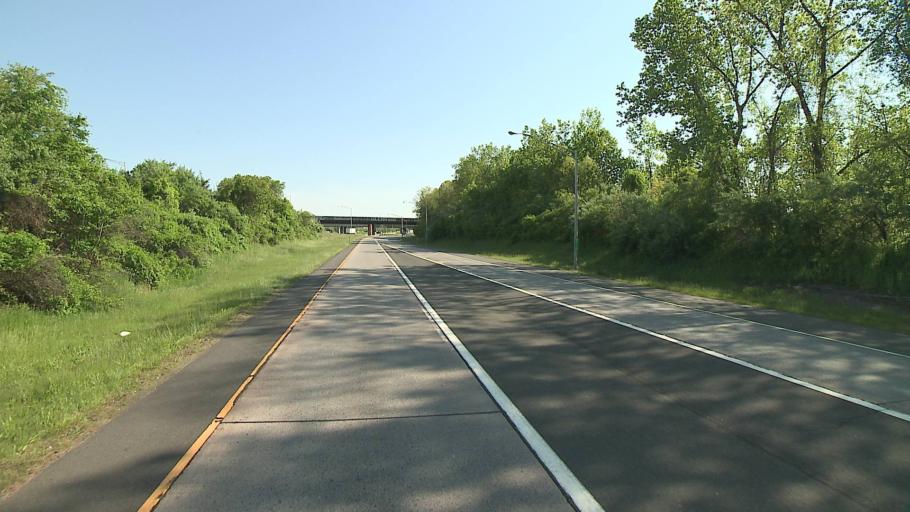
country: US
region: Connecticut
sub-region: Hartford County
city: Manchester
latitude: 41.7927
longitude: -72.5601
